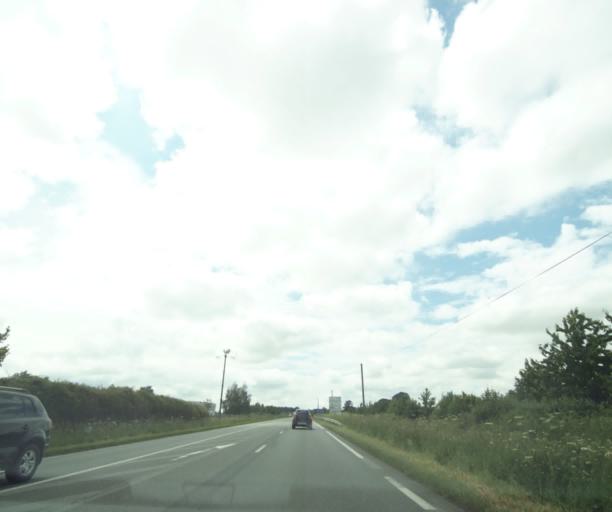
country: FR
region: Poitou-Charentes
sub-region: Departement des Deux-Sevres
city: Saint-Pardoux
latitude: 46.5520
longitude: -0.3097
